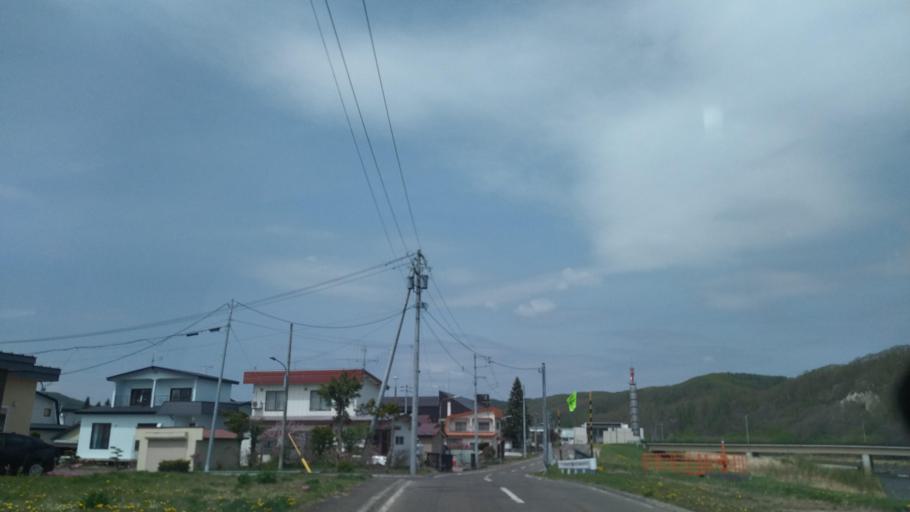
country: JP
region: Hokkaido
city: Otofuke
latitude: 43.2412
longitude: 143.5549
